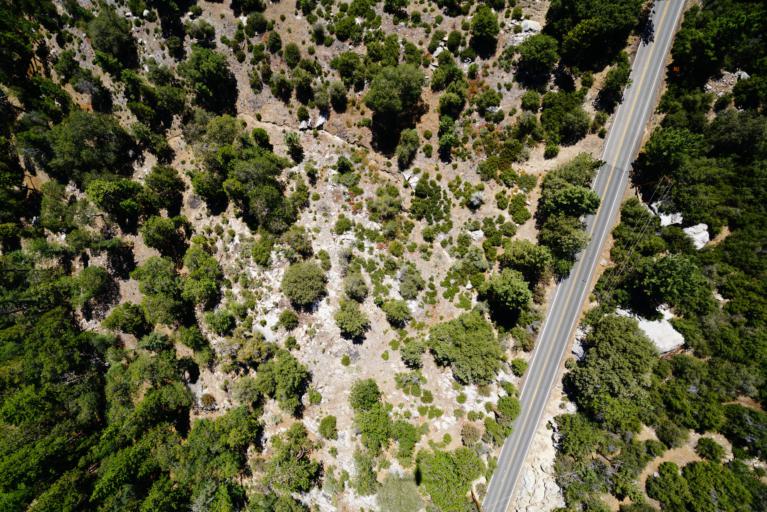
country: US
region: California
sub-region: Riverside County
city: Idyllwild-Pine Cove
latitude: 33.7480
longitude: -116.7350
